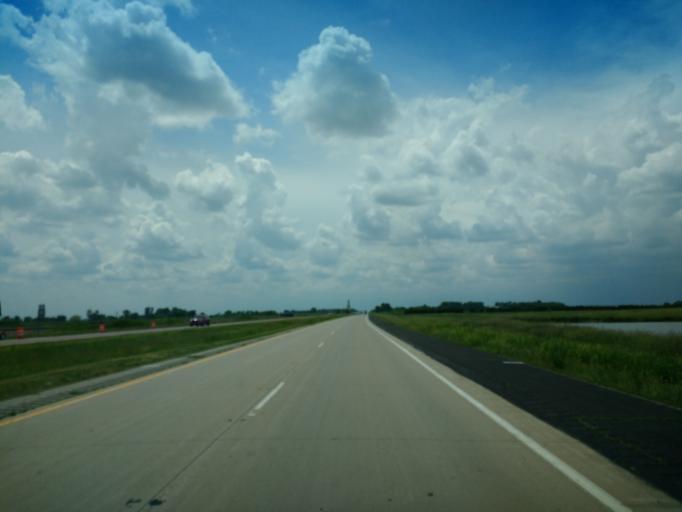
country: US
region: Minnesota
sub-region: Jackson County
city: Lakefield
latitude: 43.7851
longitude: -95.3387
